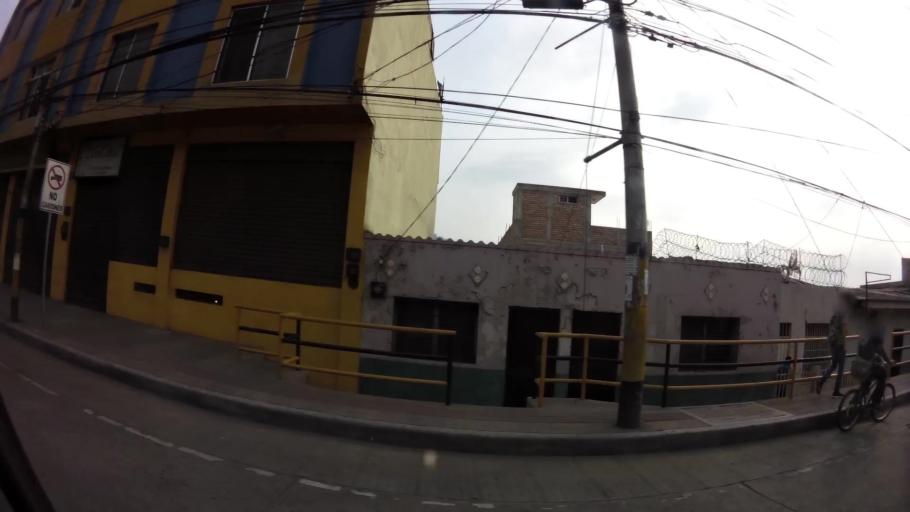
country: HN
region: Francisco Morazan
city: Tegucigalpa
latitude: 14.0974
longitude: -87.2003
